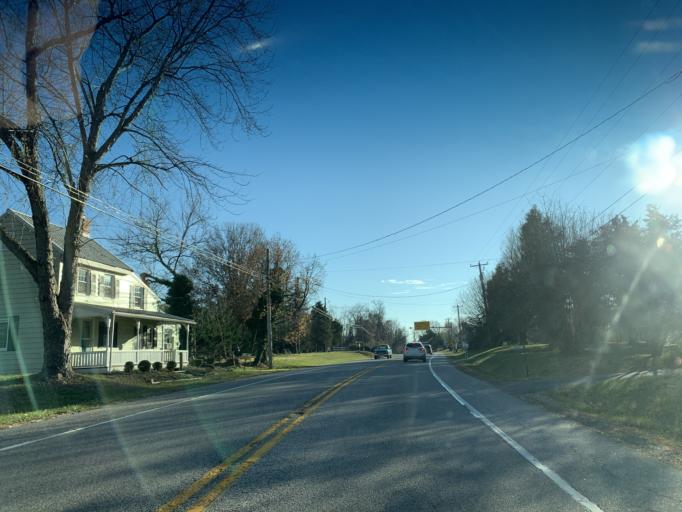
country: US
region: Delaware
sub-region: New Castle County
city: Middletown
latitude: 39.3695
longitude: -75.8831
